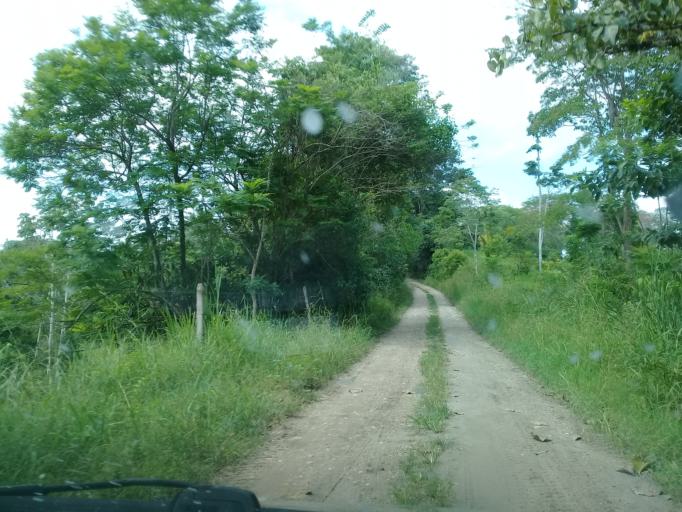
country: CO
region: Antioquia
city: Puerto Triunfo
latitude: 5.6960
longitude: -74.5535
